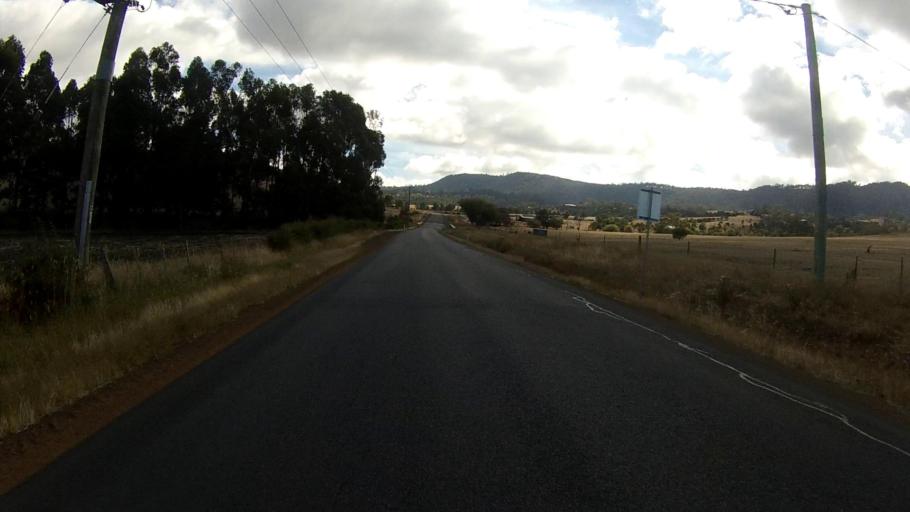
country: AU
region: Tasmania
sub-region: Brighton
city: Old Beach
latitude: -42.7685
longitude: 147.2962
